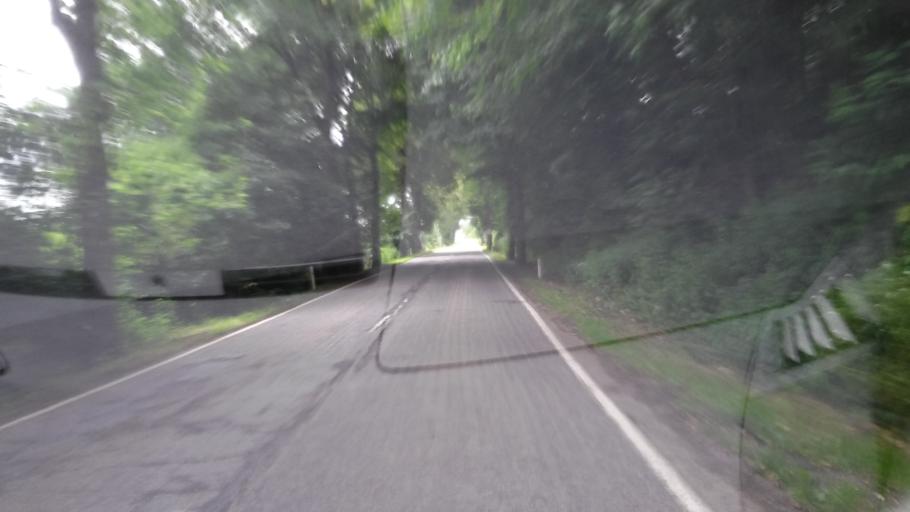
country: BE
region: Wallonia
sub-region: Province du Luxembourg
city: Arlon
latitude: 49.6943
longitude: 5.8458
